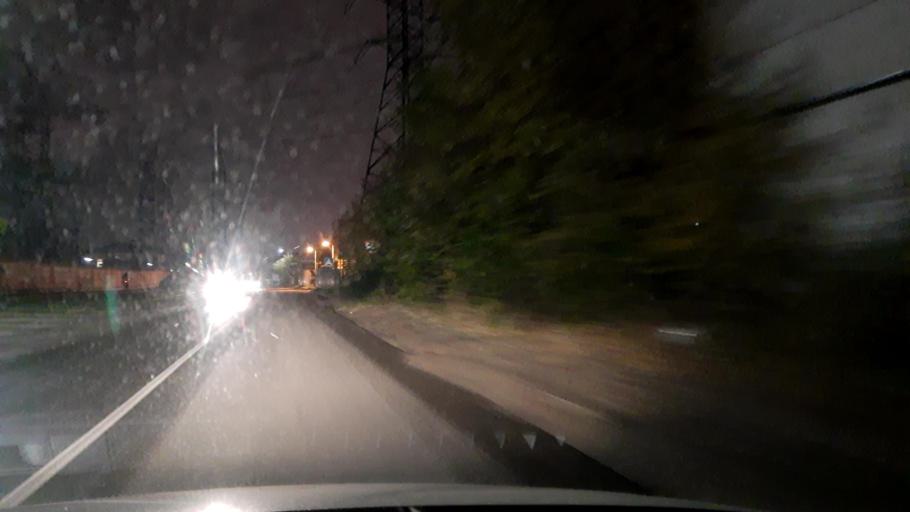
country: RU
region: Moskovskaya
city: Alekseyevka
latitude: 55.6353
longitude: 37.8143
